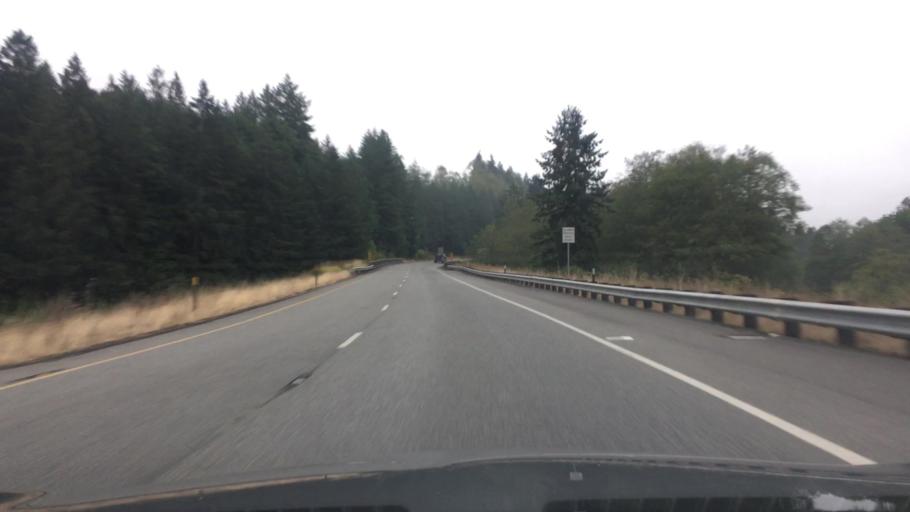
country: US
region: Washington
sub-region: Jefferson County
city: Port Hadlock-Irondale
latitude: 47.9532
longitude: -122.8841
